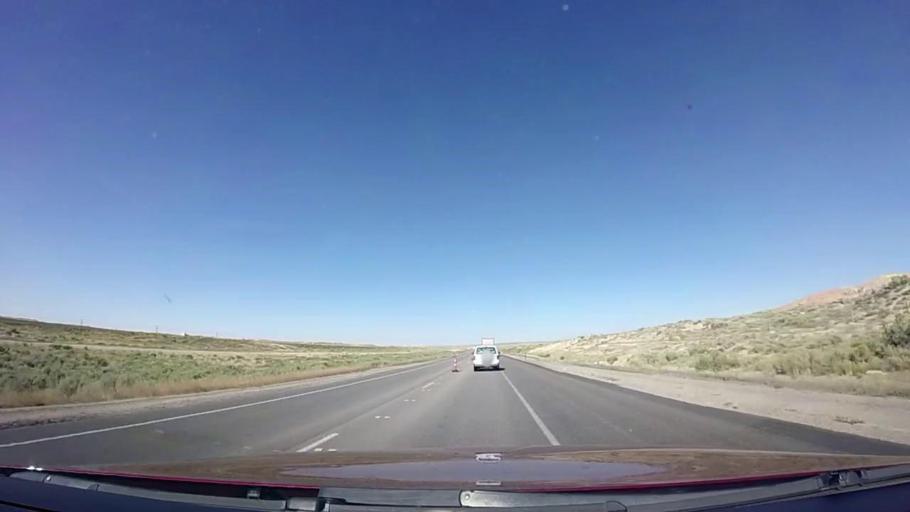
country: US
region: Wyoming
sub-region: Carbon County
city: Rawlins
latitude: 41.7064
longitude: -107.8704
